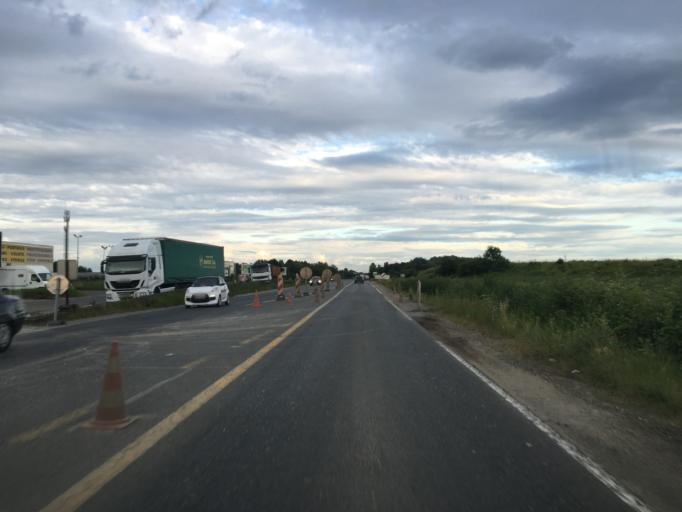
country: FR
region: Ile-de-France
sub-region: Departement de Seine-et-Marne
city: Servon
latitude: 48.7068
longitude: 2.5895
